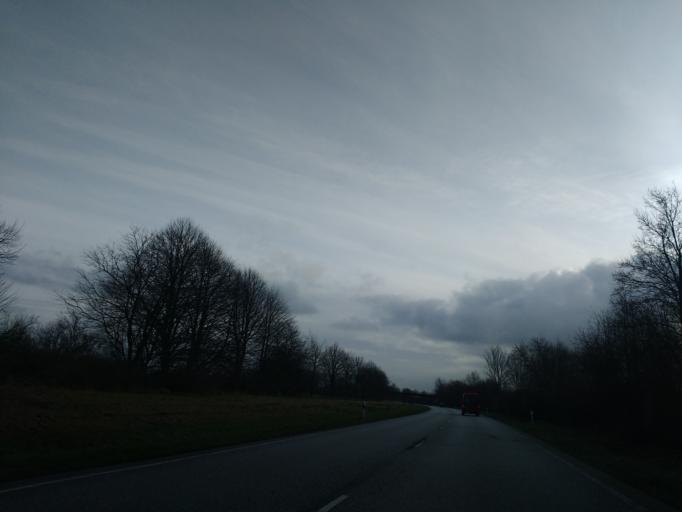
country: DE
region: Schleswig-Holstein
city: Krogaspe
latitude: 54.1271
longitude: 9.9224
